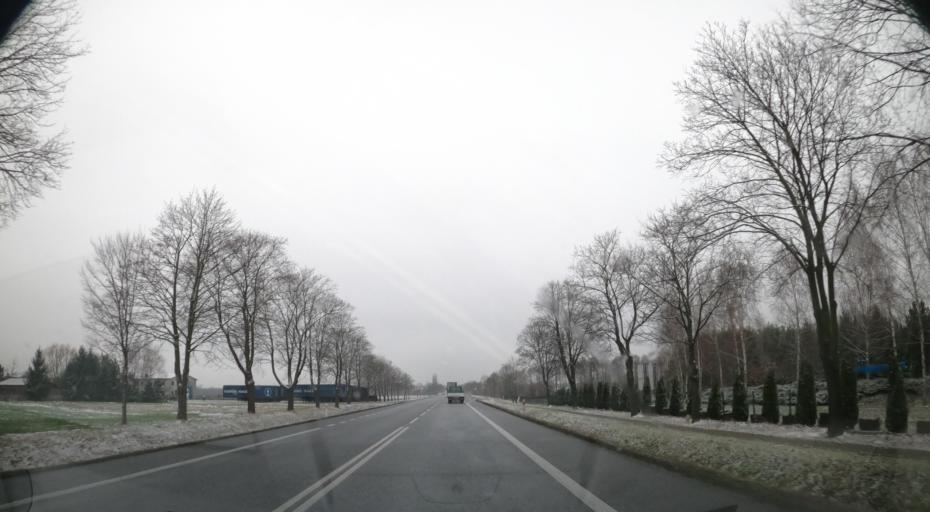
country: PL
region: Masovian Voivodeship
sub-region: Powiat sochaczewski
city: Paprotnia
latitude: 52.2104
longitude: 20.4467
